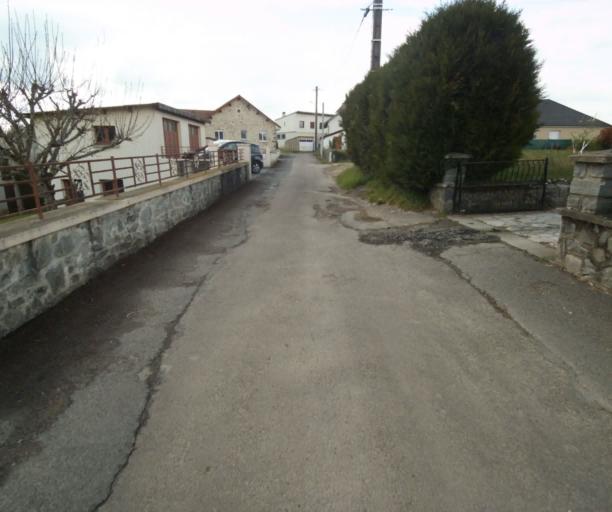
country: FR
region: Limousin
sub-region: Departement de la Correze
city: Tulle
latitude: 45.2563
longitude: 1.7453
